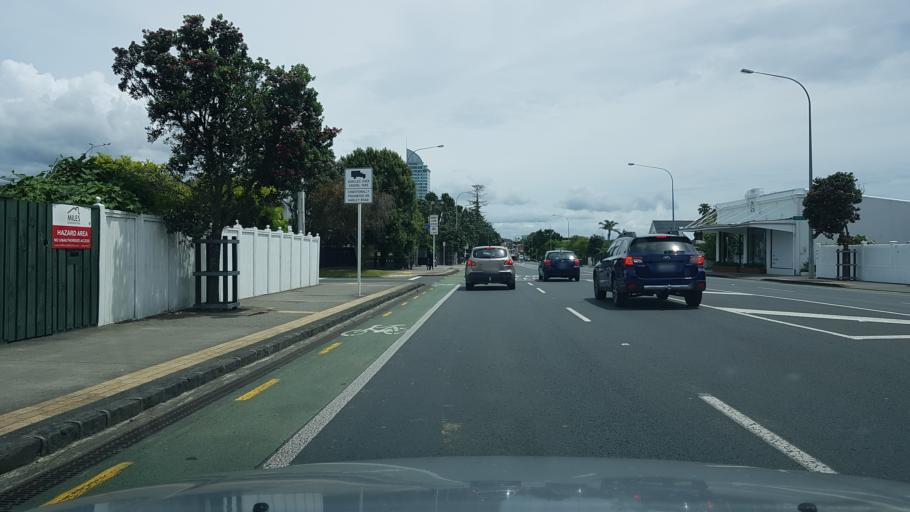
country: NZ
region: Auckland
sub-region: Auckland
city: North Shore
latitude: -36.7953
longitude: 174.7771
